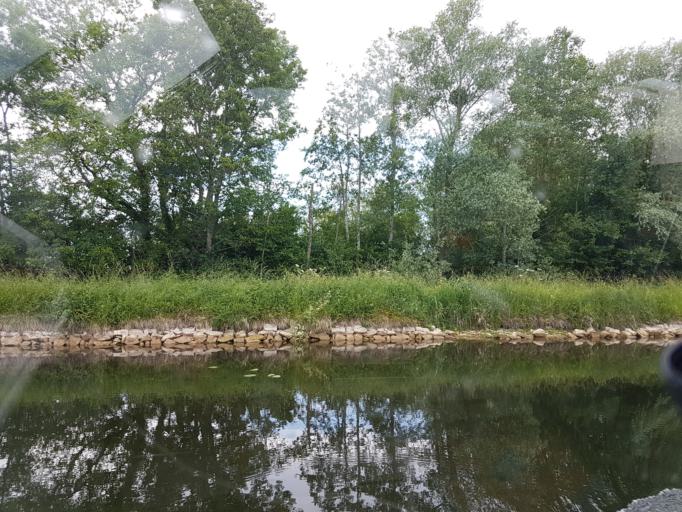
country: FR
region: Bourgogne
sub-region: Departement de l'Yonne
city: Moneteau
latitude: 47.8409
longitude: 3.5749
